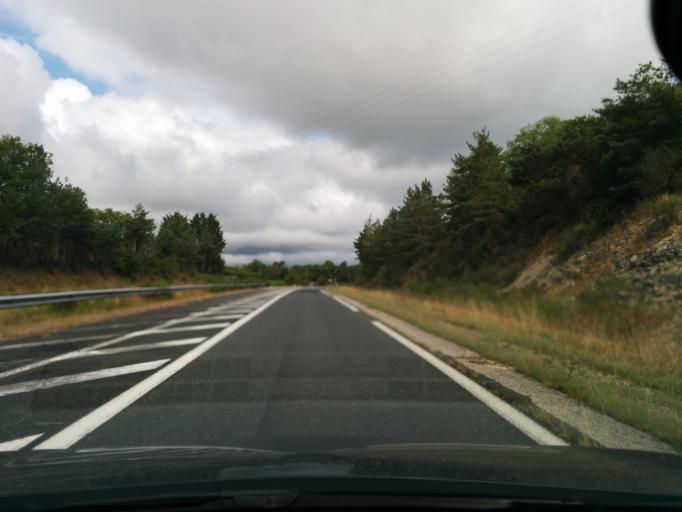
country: FR
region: Midi-Pyrenees
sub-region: Departement du Lot
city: Souillac
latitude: 44.8348
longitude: 1.4631
